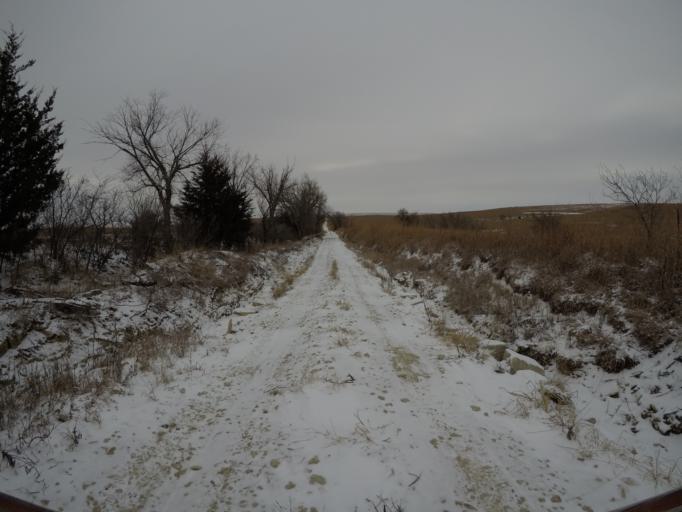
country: US
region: Kansas
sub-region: Wabaunsee County
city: Alma
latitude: 38.8975
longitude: -96.1136
